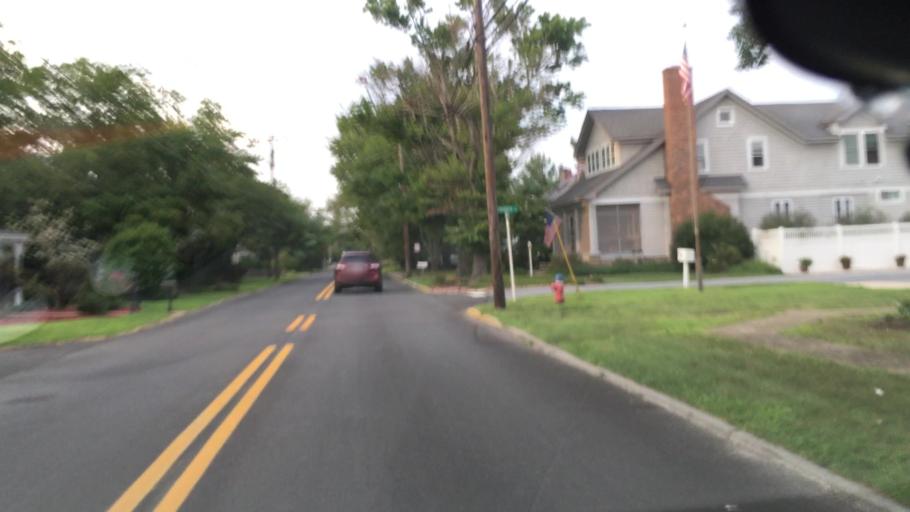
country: US
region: Delaware
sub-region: Sussex County
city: Ocean View
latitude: 38.5454
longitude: -75.0904
